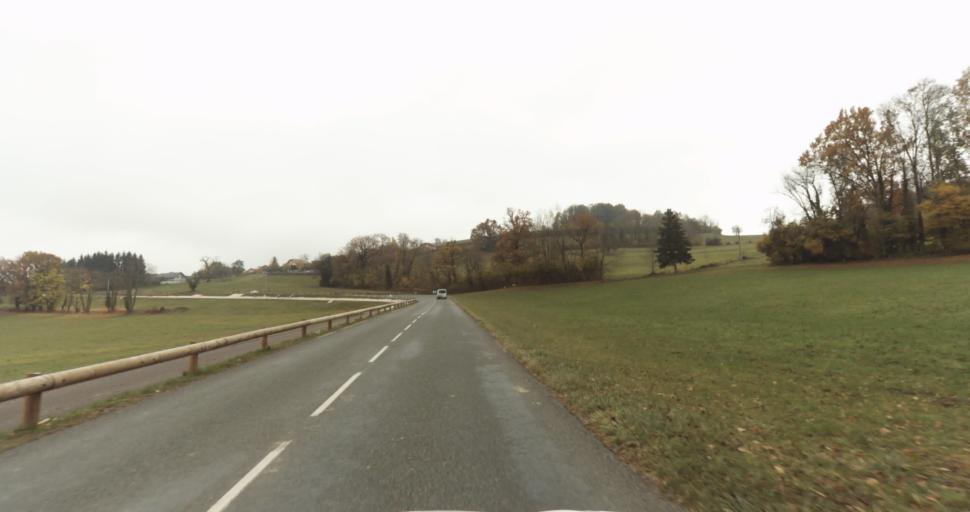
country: FR
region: Rhone-Alpes
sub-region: Departement de la Haute-Savoie
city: Alby-sur-Cheran
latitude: 45.8022
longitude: 6.0102
